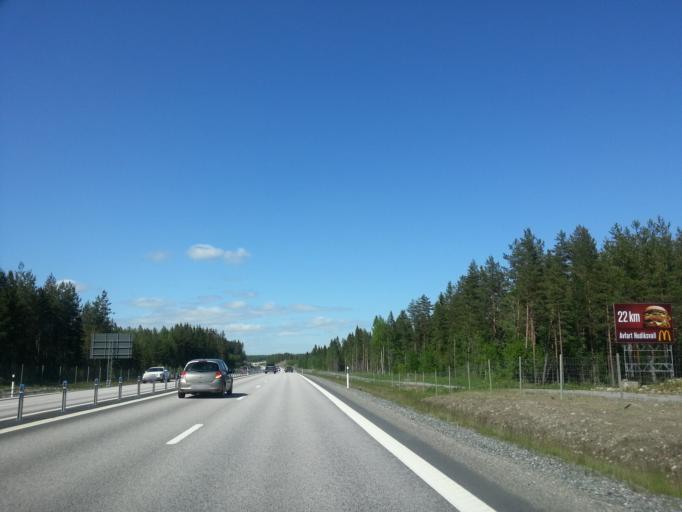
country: SE
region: Gaevleborg
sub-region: Hudiksvalls Kommun
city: Iggesund
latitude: 61.5644
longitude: 16.9751
